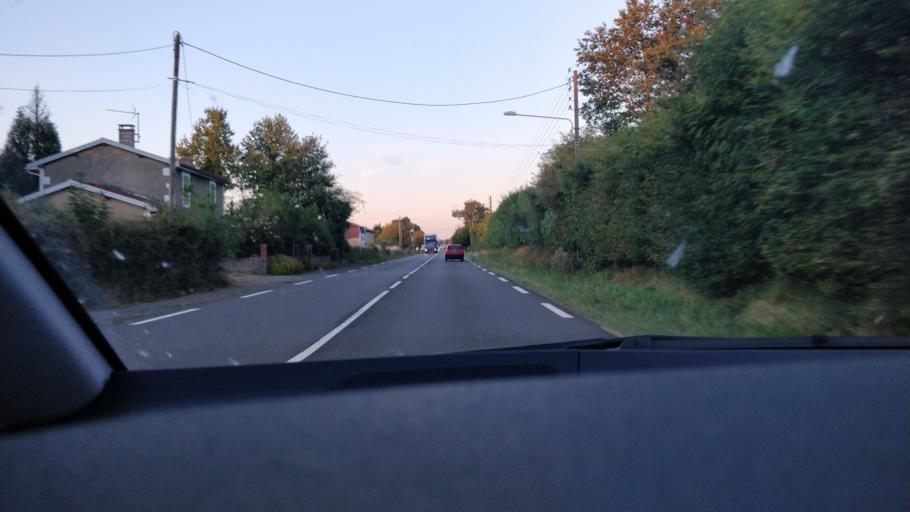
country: FR
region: Poitou-Charentes
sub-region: Departement de la Charente
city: Loubert
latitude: 45.8713
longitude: 0.5516
